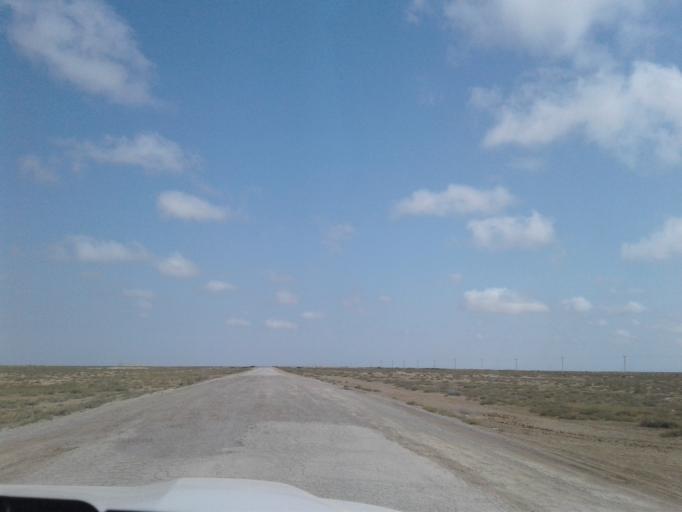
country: IR
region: Golestan
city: Gomishan
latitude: 37.6526
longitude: 53.9321
